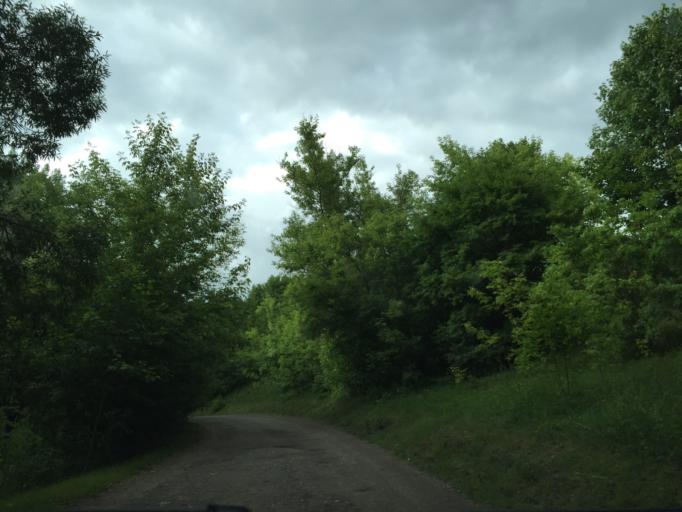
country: PL
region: Podlasie
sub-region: Suwalki
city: Suwalki
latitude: 54.1173
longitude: 22.9243
